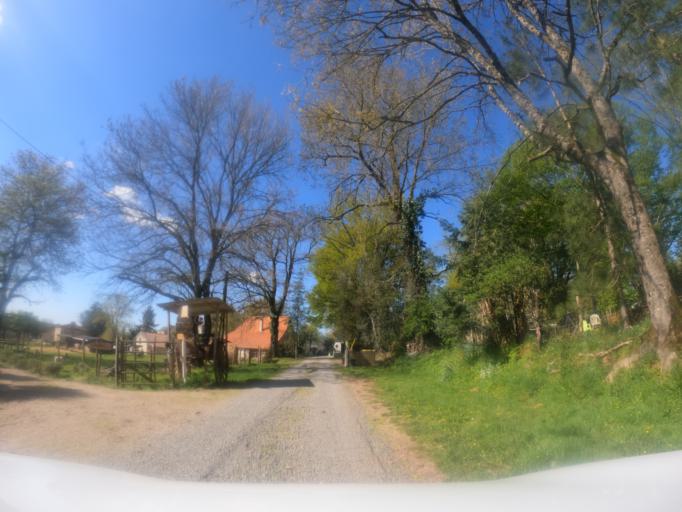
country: FR
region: Pays de la Loire
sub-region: Departement de la Vendee
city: Saint-Vincent-sur-Graon
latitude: 46.5171
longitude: -1.3701
